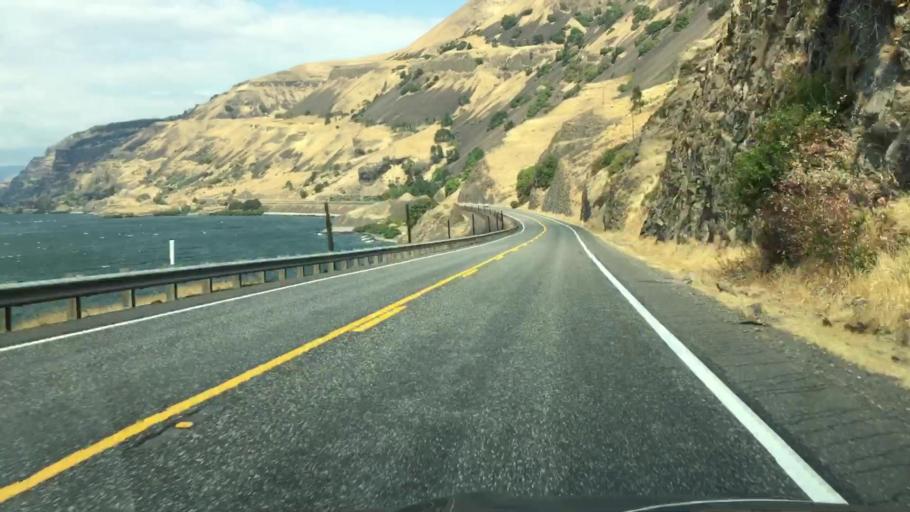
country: US
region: Oregon
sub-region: Wasco County
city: Chenoweth
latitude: 45.6693
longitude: -121.2079
